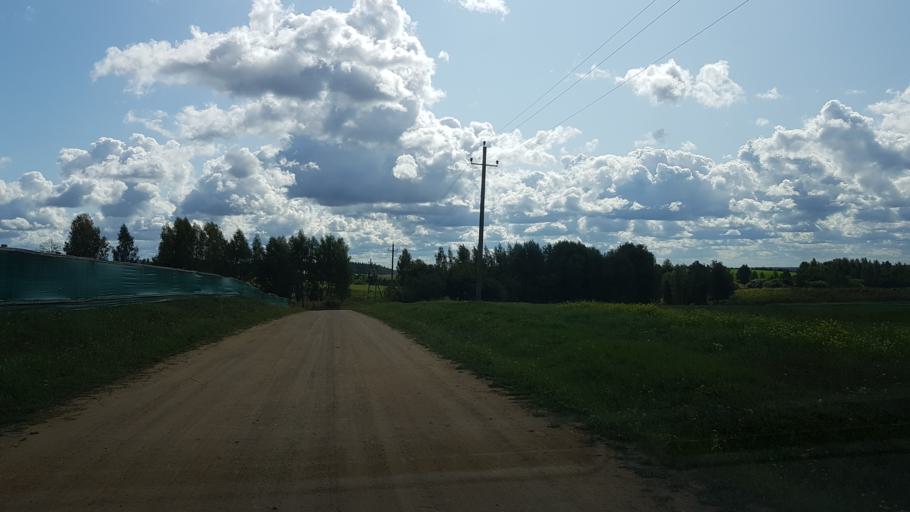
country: BY
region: Minsk
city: Dzyarzhynsk
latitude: 53.7584
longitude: 27.2057
